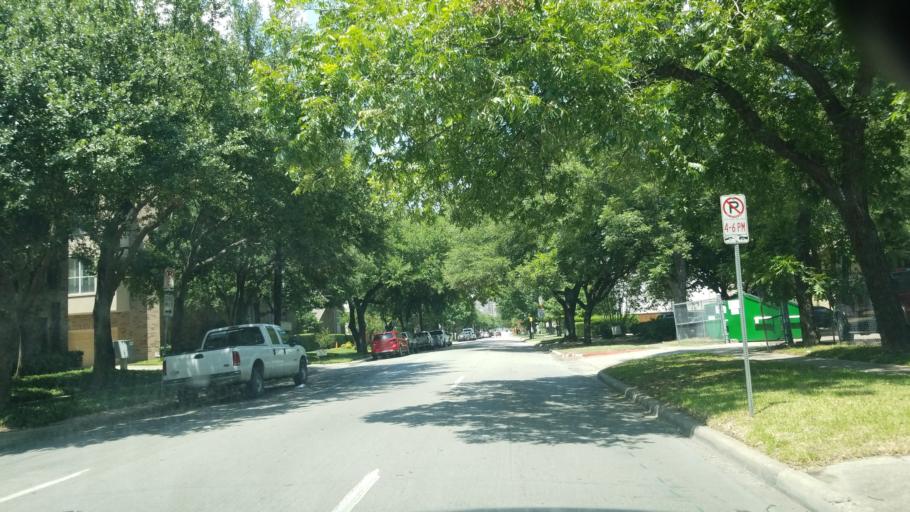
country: US
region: Texas
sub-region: Dallas County
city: Highland Park
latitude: 32.8168
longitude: -96.7907
